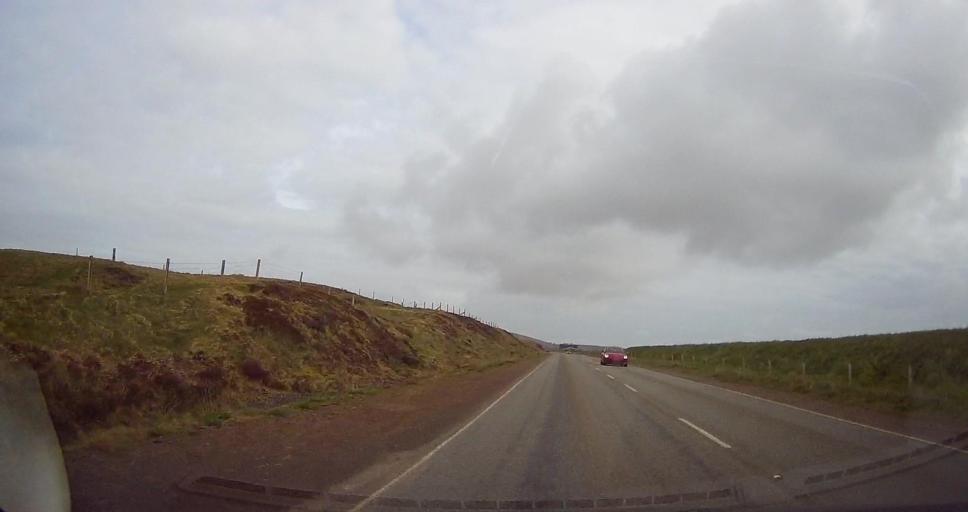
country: GB
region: Scotland
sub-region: Shetland Islands
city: Lerwick
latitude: 60.1161
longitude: -1.2176
